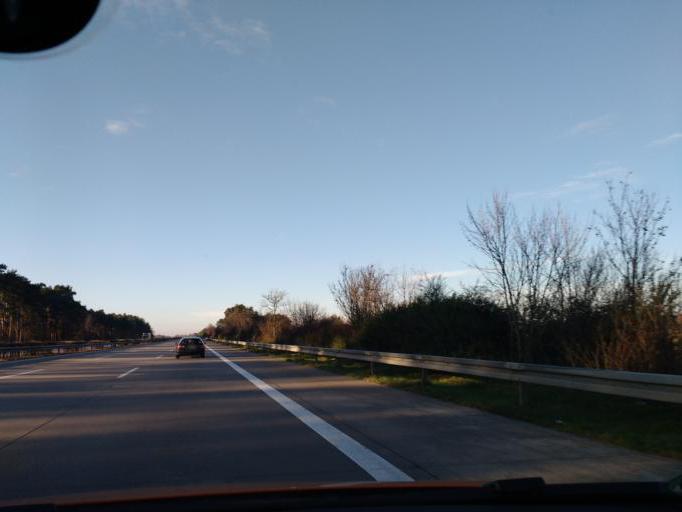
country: DE
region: Brandenburg
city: Ziesar
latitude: 52.2666
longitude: 12.3531
